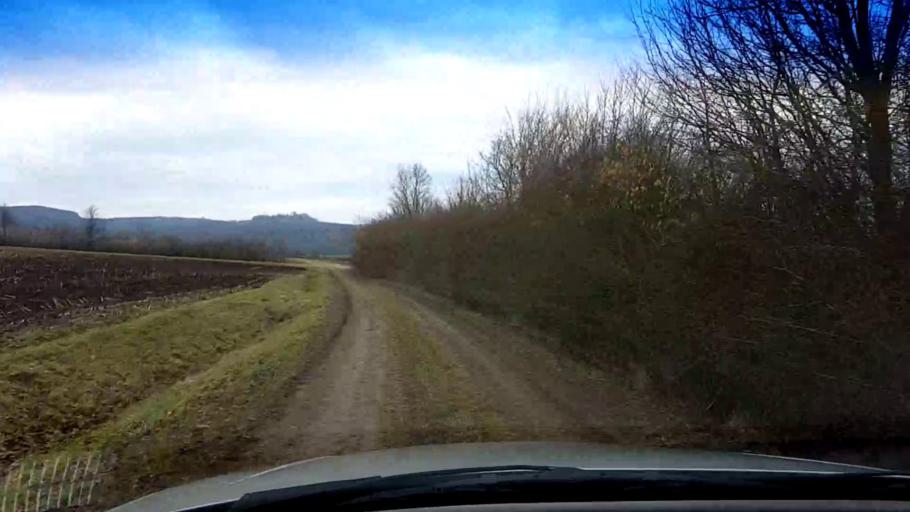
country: DE
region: Bavaria
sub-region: Upper Franconia
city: Schesslitz
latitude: 49.9834
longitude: 11.0223
